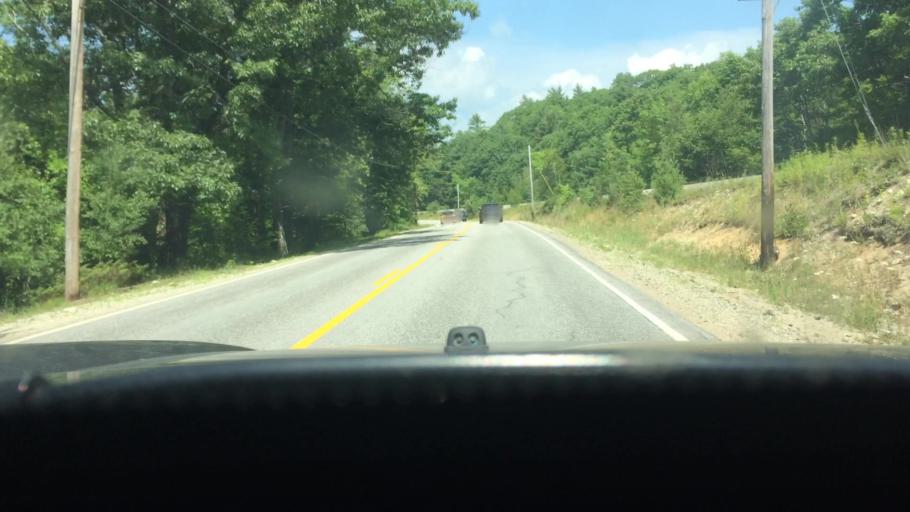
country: US
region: Maine
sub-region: Androscoggin County
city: Mechanic Falls
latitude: 44.1239
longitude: -70.4326
